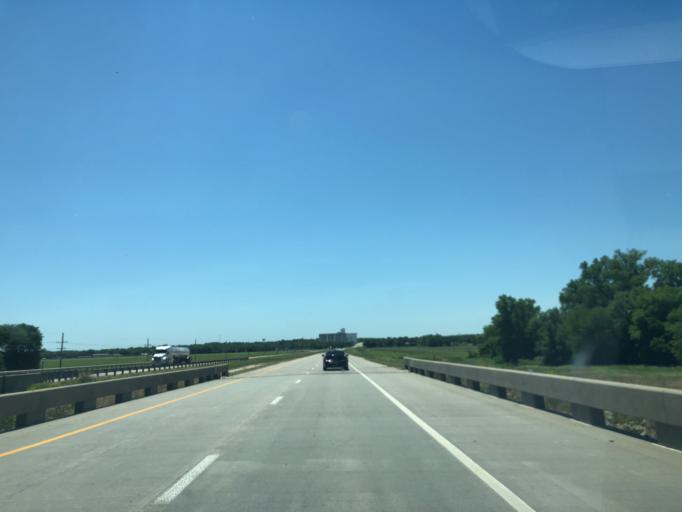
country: US
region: Kansas
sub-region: Cloud County
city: Concordia
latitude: 39.5893
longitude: -97.6588
